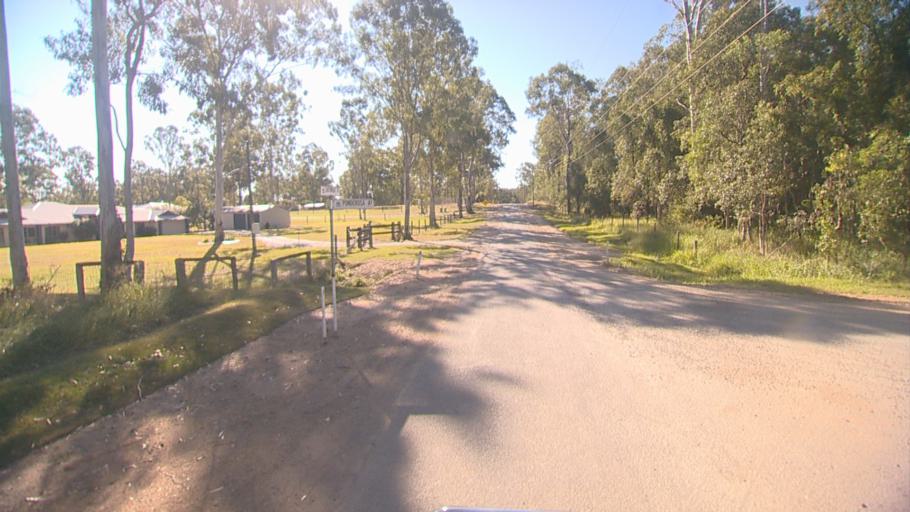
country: AU
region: Queensland
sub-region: Logan
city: Windaroo
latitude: -27.7611
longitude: 153.1511
